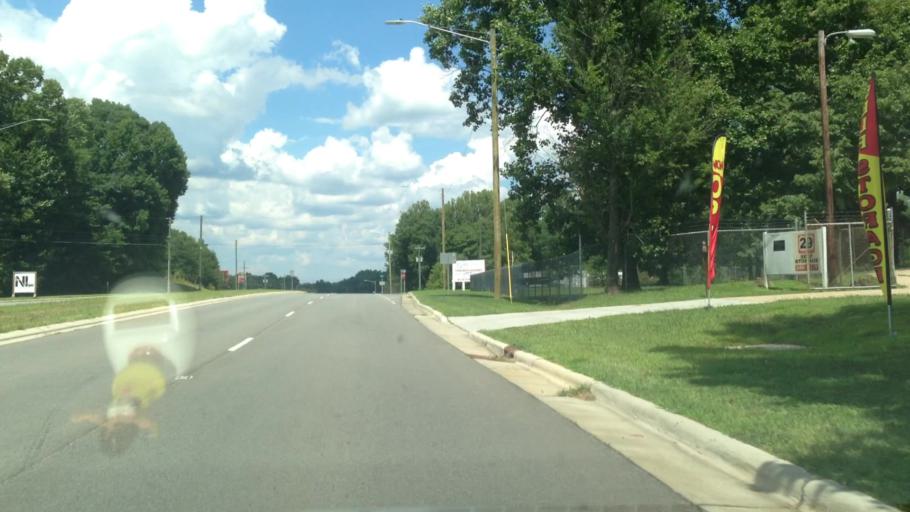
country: US
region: North Carolina
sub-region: Rockingham County
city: Reidsville
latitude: 36.3738
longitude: -79.6748
